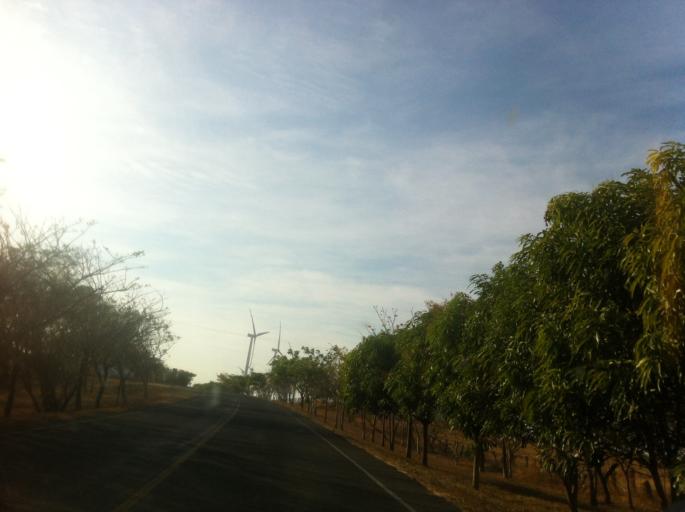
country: NI
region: Rivas
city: San Jorge
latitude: 11.3117
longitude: -85.7026
